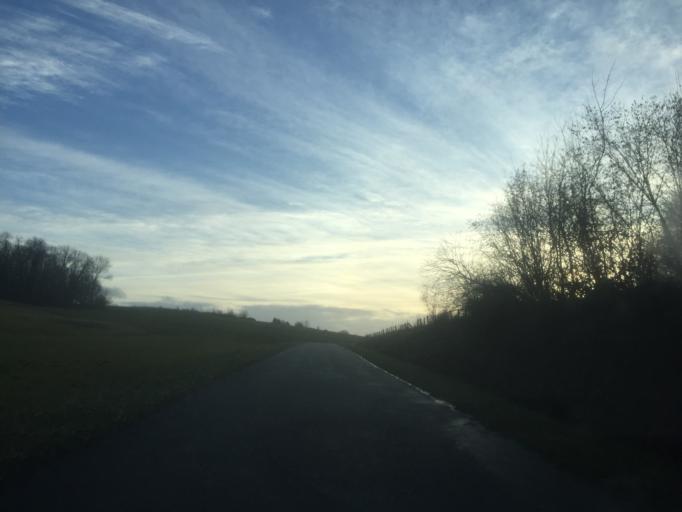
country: FR
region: Franche-Comte
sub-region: Departement du Jura
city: Dampierre
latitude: 47.1320
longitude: 5.7149
